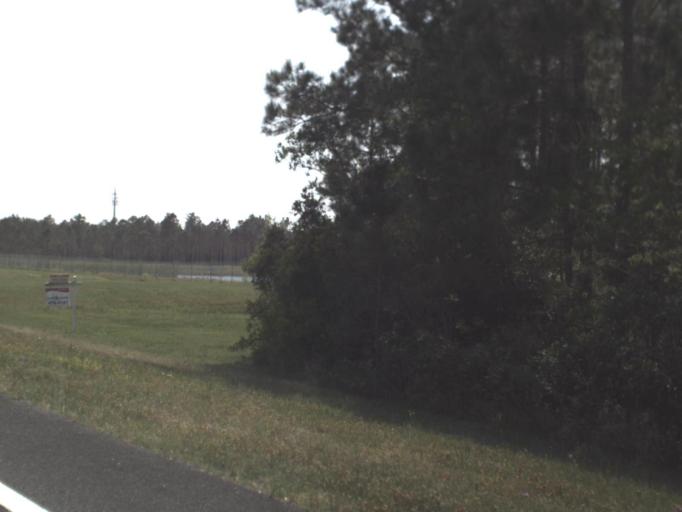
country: US
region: Florida
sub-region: Santa Rosa County
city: Tiger Point
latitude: 30.4917
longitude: -87.0802
